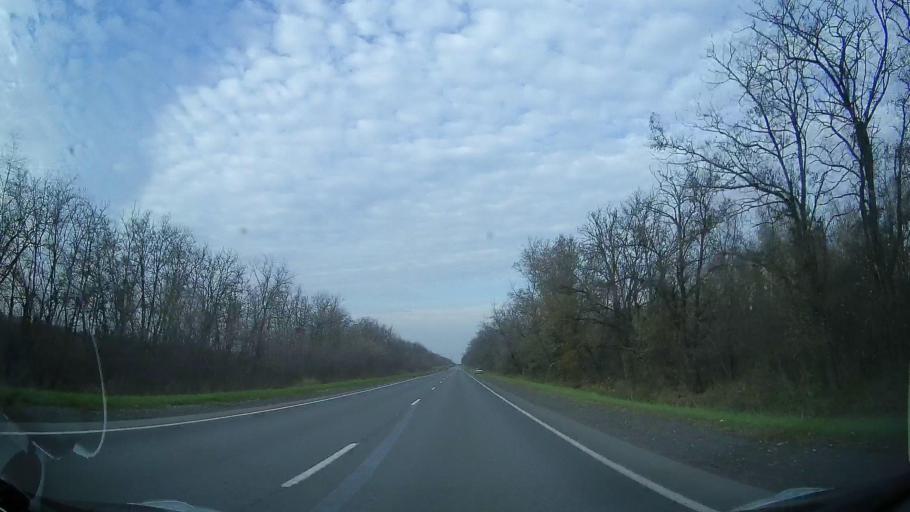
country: RU
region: Rostov
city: Bagayevskaya
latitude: 47.1140
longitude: 40.2767
